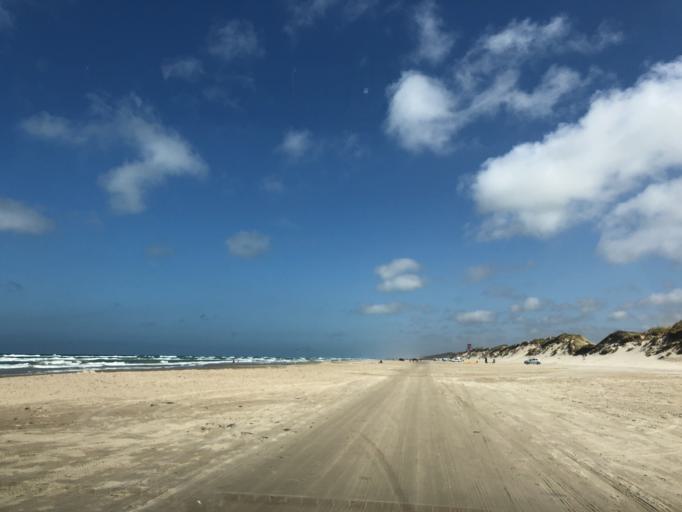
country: DK
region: North Denmark
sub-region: Jammerbugt Kommune
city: Pandrup
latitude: 57.2482
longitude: 9.5710
